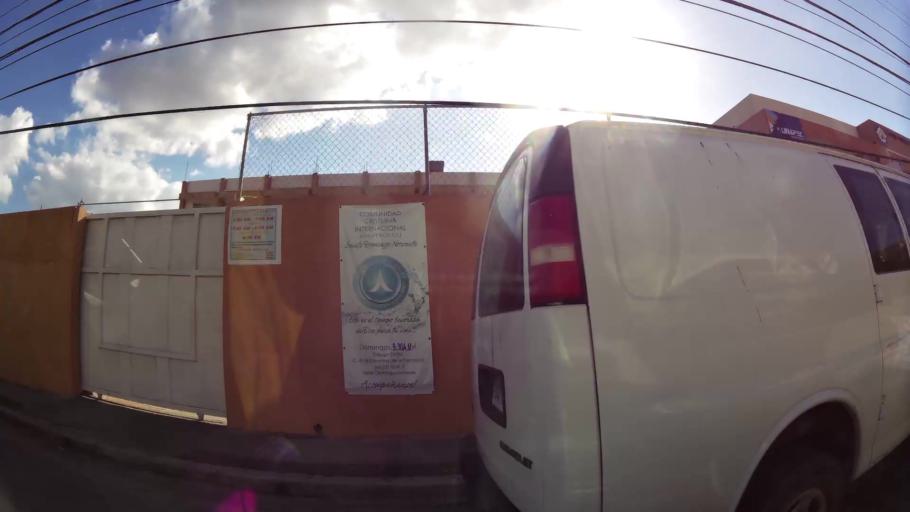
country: DO
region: Nacional
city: Santo Domingo
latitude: 18.5114
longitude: -69.9795
